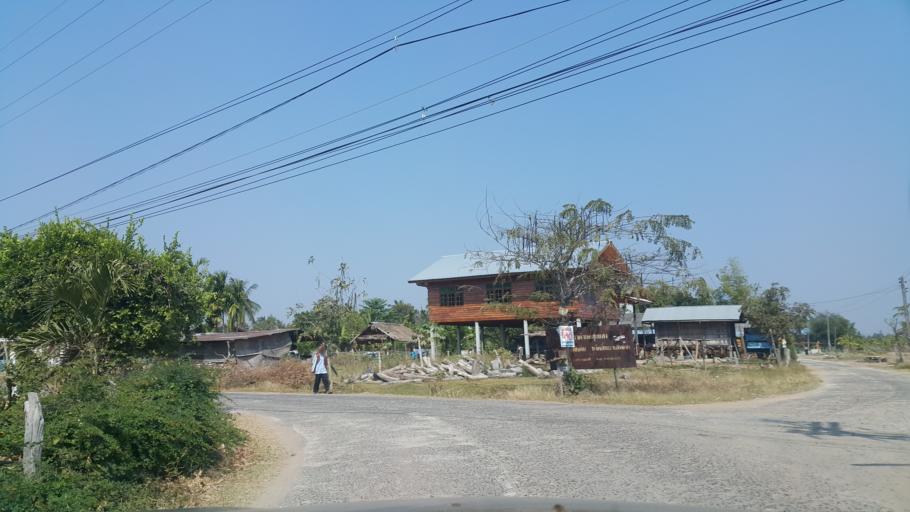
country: TH
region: Buriram
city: Satuek
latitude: 15.1370
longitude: 103.3450
